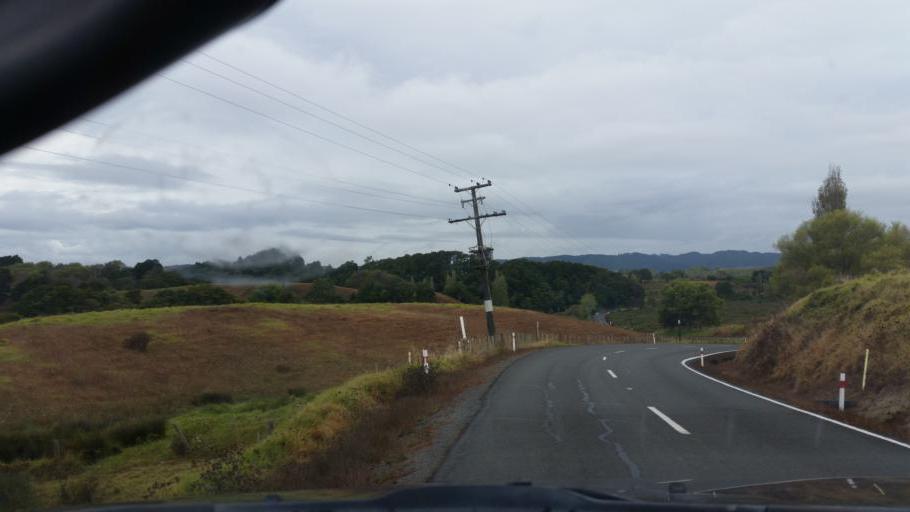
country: NZ
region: Auckland
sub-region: Auckland
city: Wellsford
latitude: -36.1249
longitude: 174.3593
